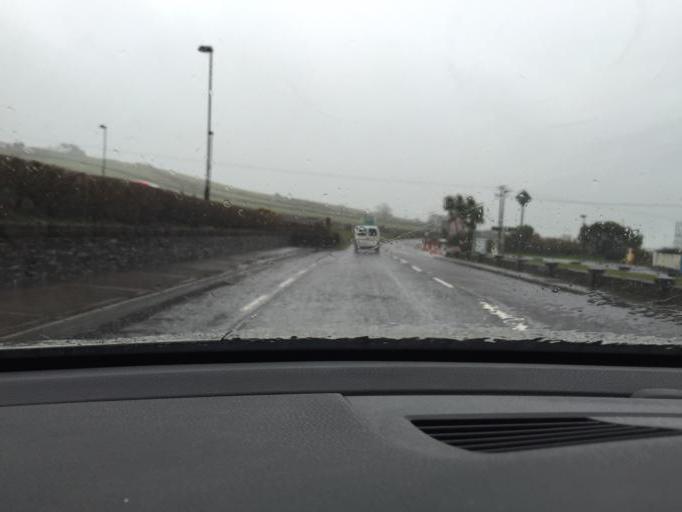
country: IE
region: Munster
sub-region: Ciarrai
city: Dingle
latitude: 52.1359
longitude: -10.2669
